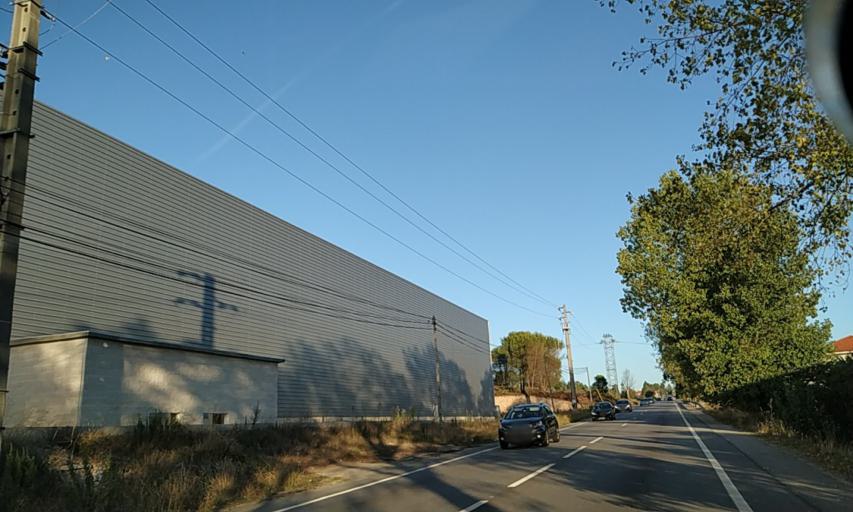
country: PT
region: Aveiro
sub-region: Oliveira do Bairro
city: Oia
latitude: 40.5552
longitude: -8.5515
